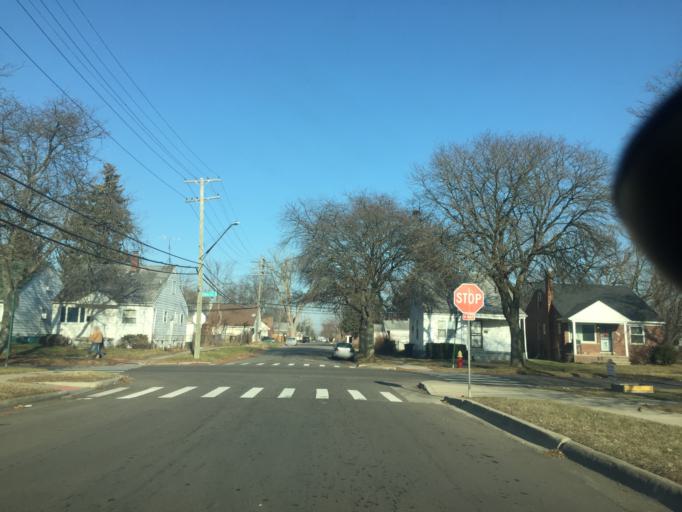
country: US
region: Michigan
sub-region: Macomb County
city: Eastpointe
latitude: 42.4425
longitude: -82.9633
